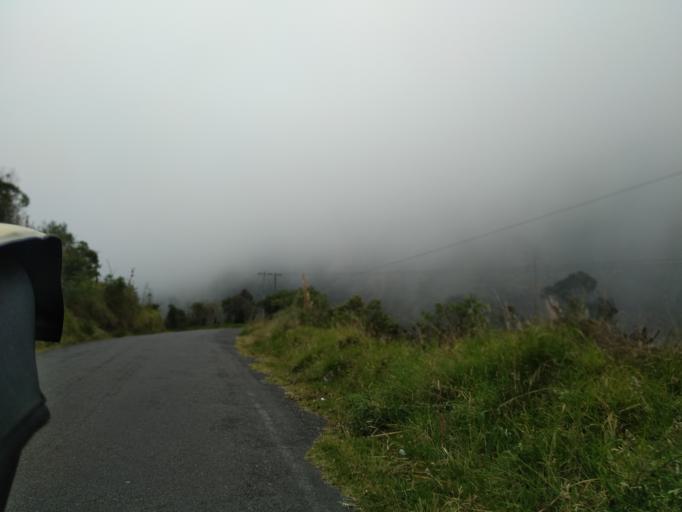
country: EC
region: Cotopaxi
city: Saquisili
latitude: -0.6942
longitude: -78.8163
